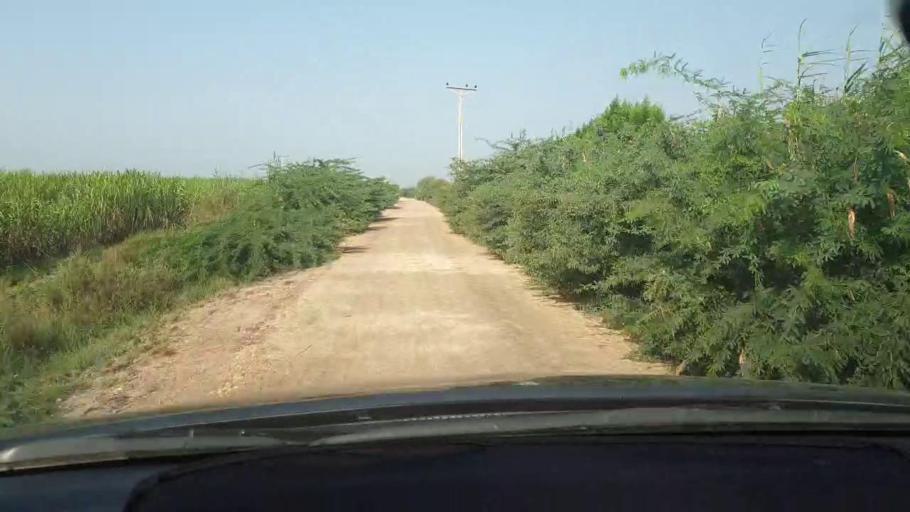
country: PK
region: Sindh
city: Tando Bago
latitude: 24.6800
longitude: 69.1313
